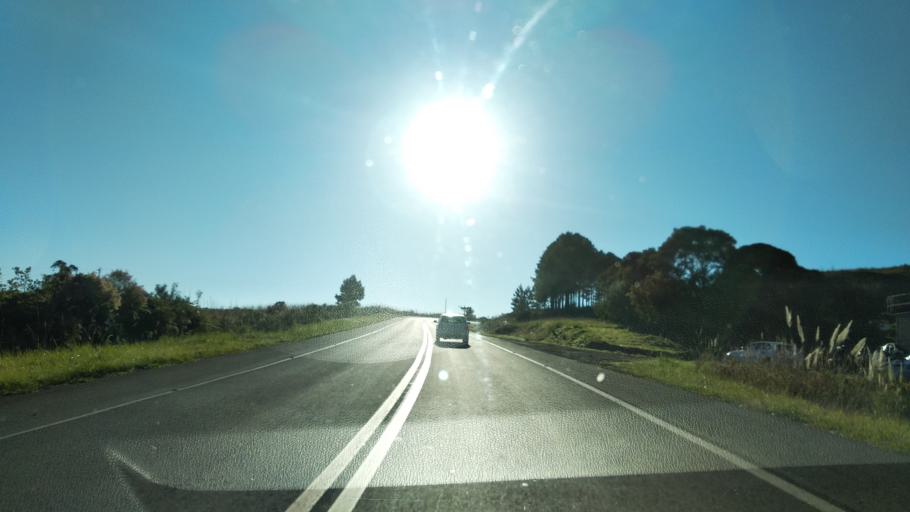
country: BR
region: Santa Catarina
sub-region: Lages
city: Lages
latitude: -27.7881
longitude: -50.4282
